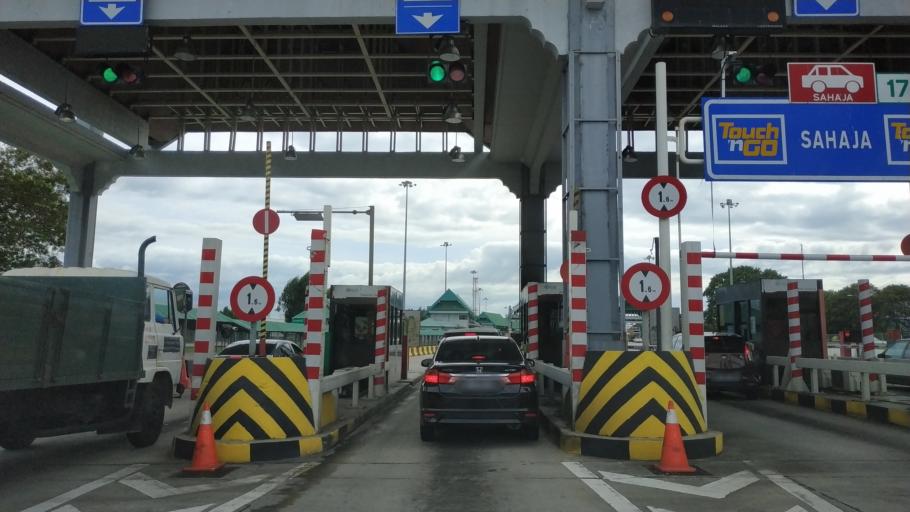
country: MY
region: Penang
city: Perai
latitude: 5.3591
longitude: 100.3944
